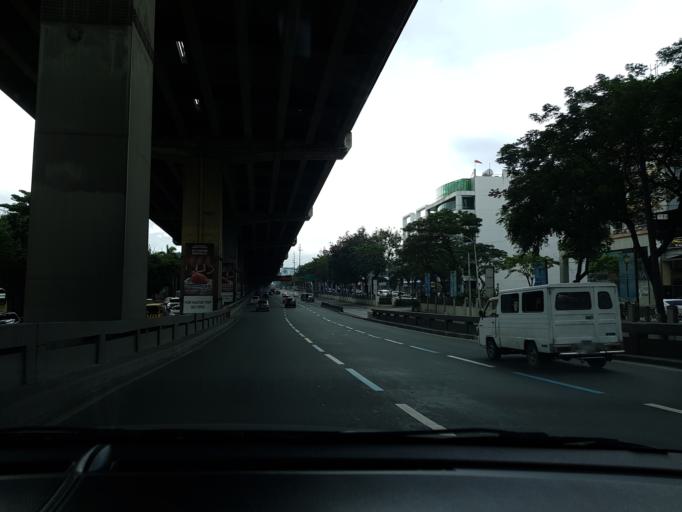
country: PH
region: Metro Manila
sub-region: Makati City
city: Makati City
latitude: 14.5386
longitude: 121.0177
